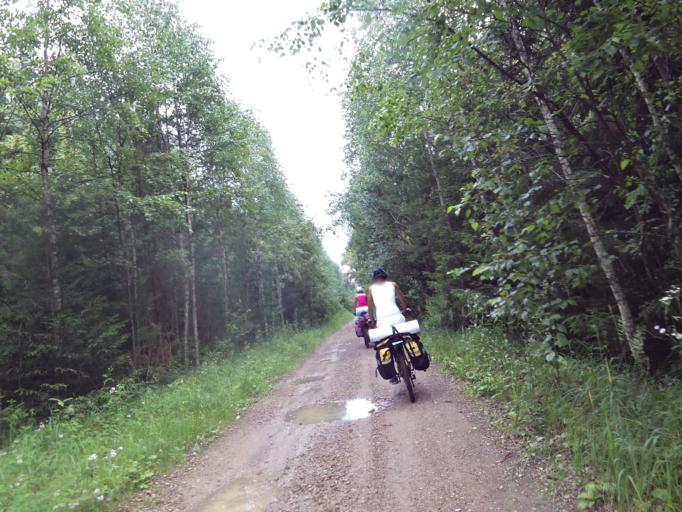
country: RU
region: Moskovskaya
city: Popovo
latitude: 54.9504
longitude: 37.6971
